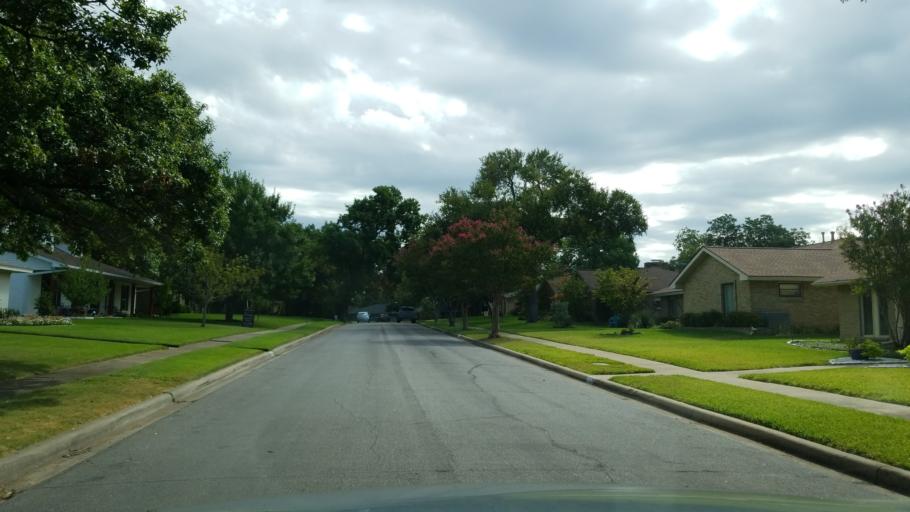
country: US
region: Texas
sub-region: Dallas County
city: Richardson
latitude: 32.9670
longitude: -96.7715
